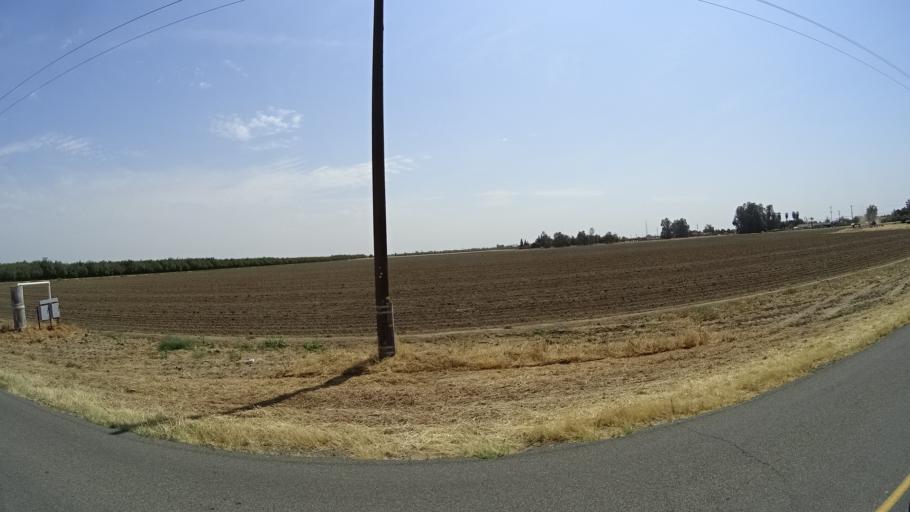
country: US
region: California
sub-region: Kings County
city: Armona
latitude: 36.3160
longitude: -119.7448
